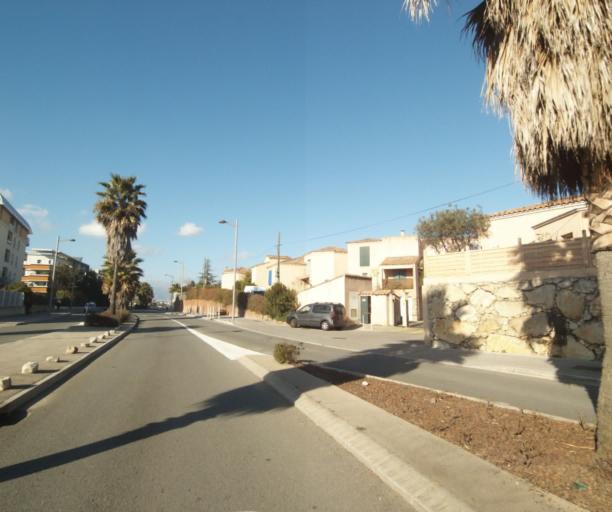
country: FR
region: Provence-Alpes-Cote d'Azur
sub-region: Departement des Alpes-Maritimes
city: Antibes
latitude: 43.5950
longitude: 7.1149
